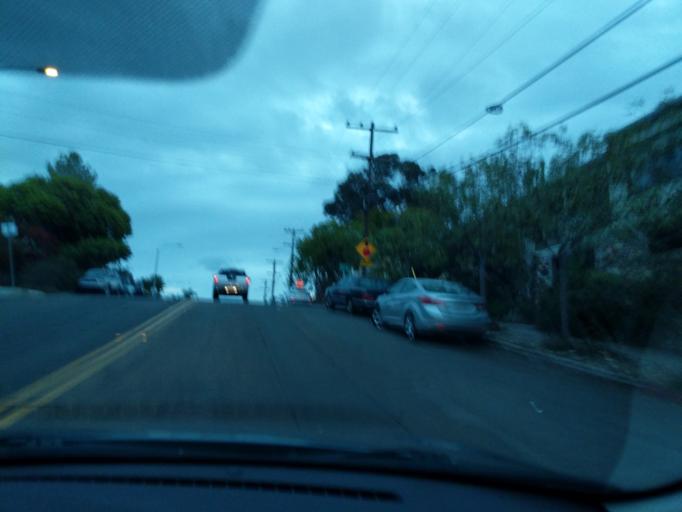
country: US
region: California
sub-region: San Diego County
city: San Diego
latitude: 32.7169
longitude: -117.1273
